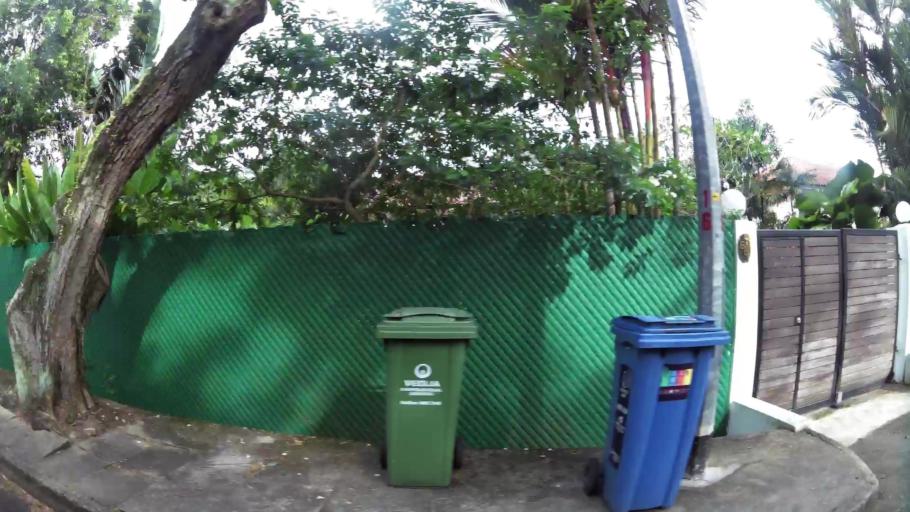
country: SG
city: Singapore
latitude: 1.3271
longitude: 103.8175
